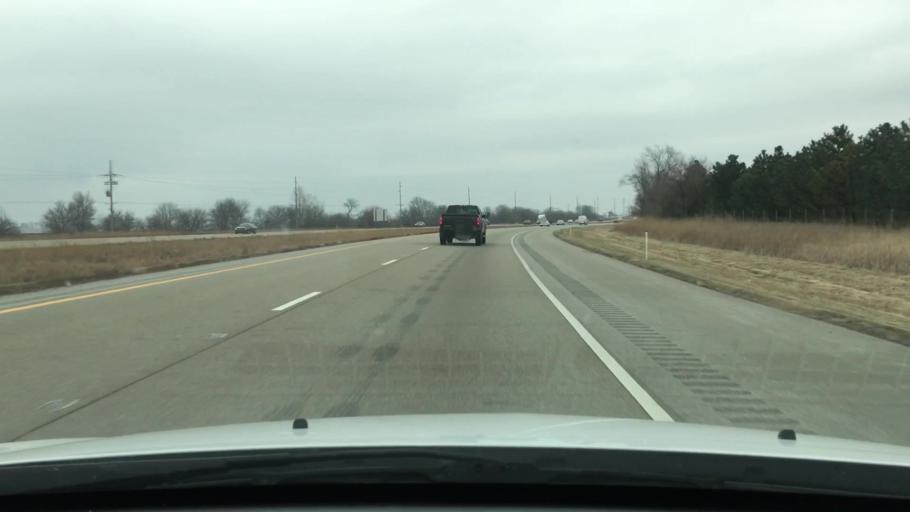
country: US
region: Illinois
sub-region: Logan County
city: Atlanta
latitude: 40.2769
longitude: -89.2115
